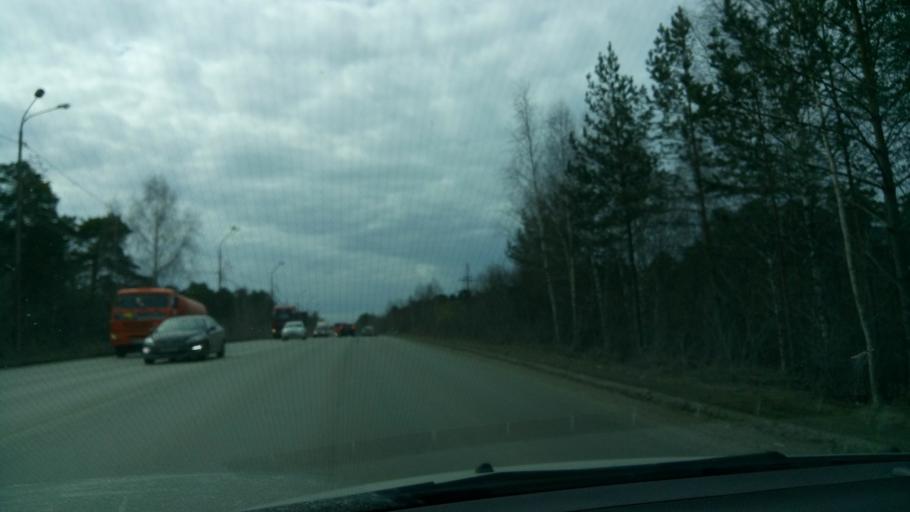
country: RU
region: Sverdlovsk
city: Beryozovsky
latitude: 56.8952
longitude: 60.7567
